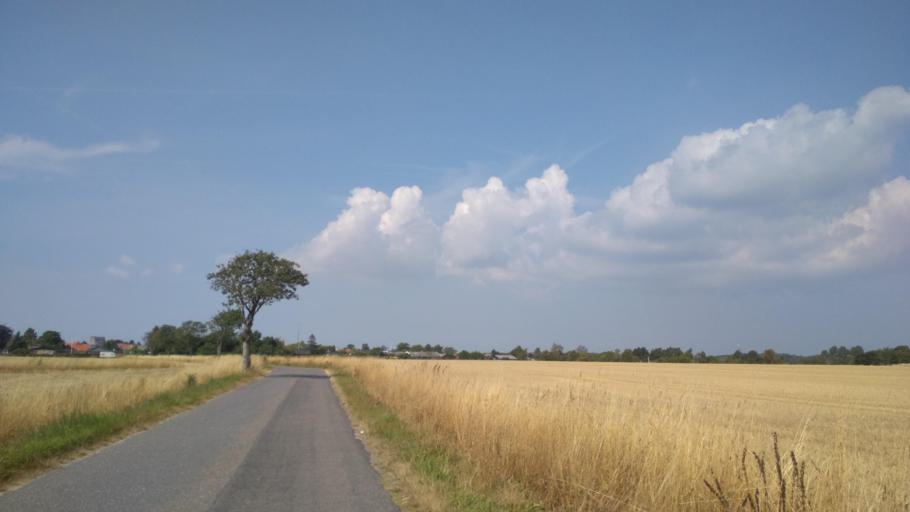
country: DK
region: Capital Region
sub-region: Bornholm Kommune
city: Akirkeby
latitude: 55.0660
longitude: 14.9334
